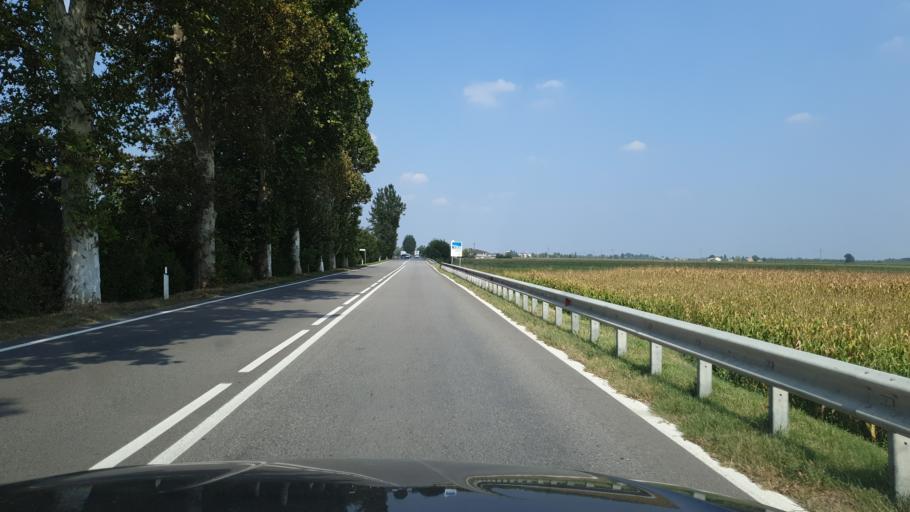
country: IT
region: Veneto
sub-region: Provincia di Rovigo
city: Bosaro
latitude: 45.0146
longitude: 11.7688
